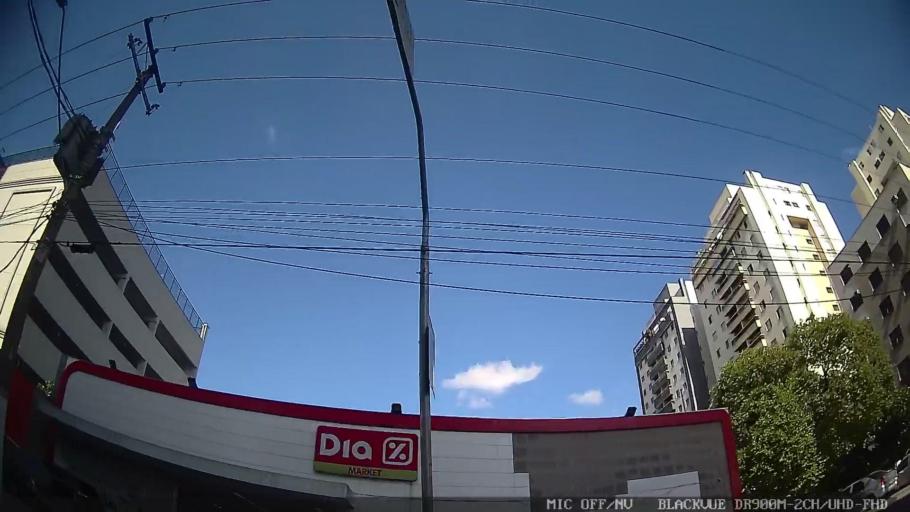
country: BR
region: Sao Paulo
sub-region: Sao Paulo
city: Sao Paulo
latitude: -23.5783
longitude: -46.6062
